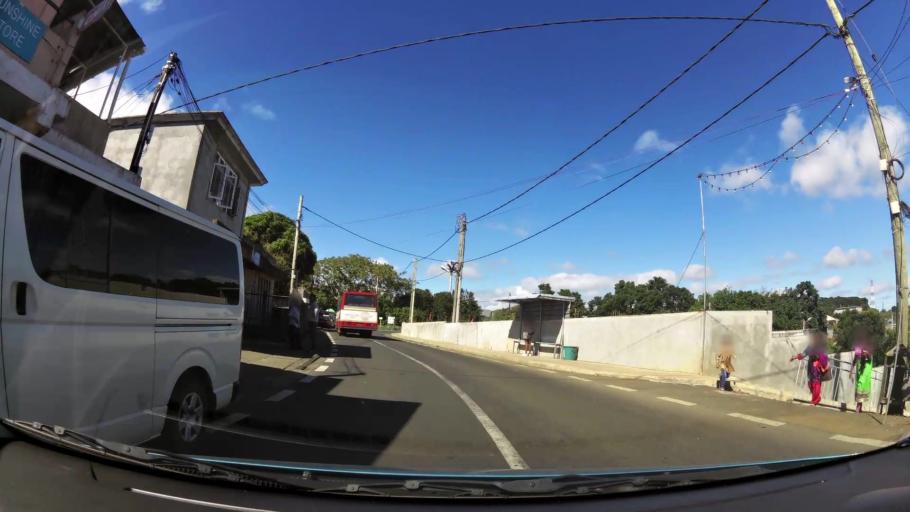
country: MU
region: Plaines Wilhems
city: Vacoas
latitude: -20.3329
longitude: 57.4752
